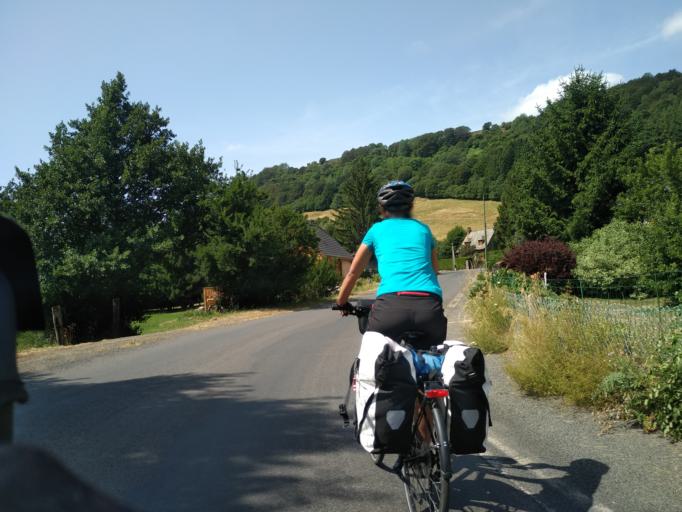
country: FR
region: Auvergne
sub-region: Departement du Cantal
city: Riom-es-Montagnes
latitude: 45.1575
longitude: 2.7047
